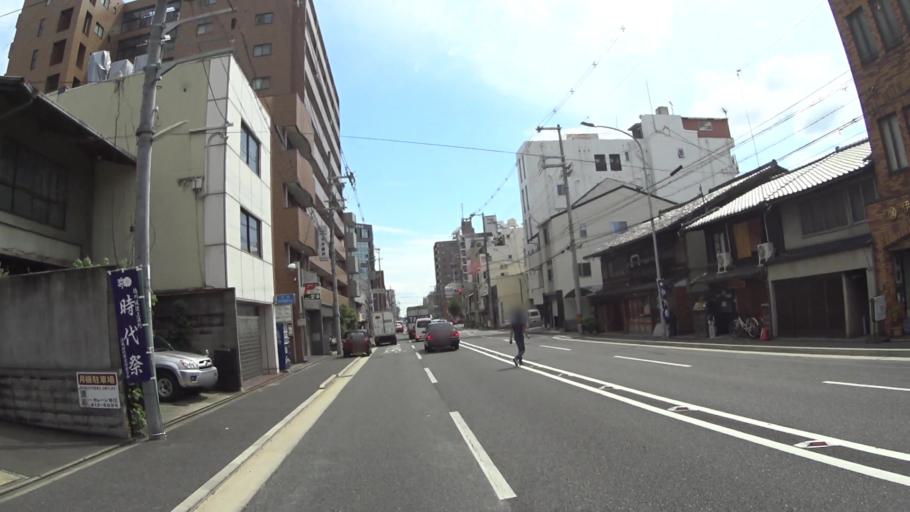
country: JP
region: Kyoto
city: Kyoto
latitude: 34.9975
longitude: 135.7492
